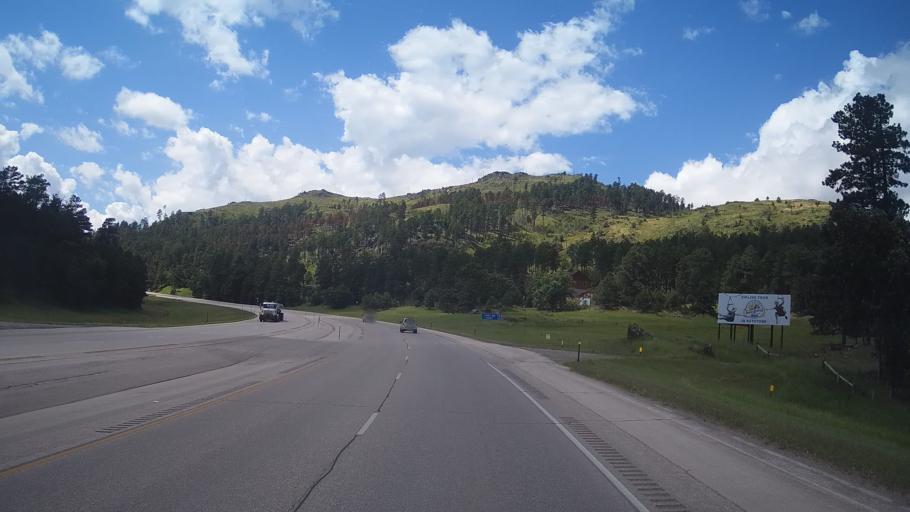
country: US
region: South Dakota
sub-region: Pennington County
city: Colonial Pine Hills
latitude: 43.9435
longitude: -103.3926
